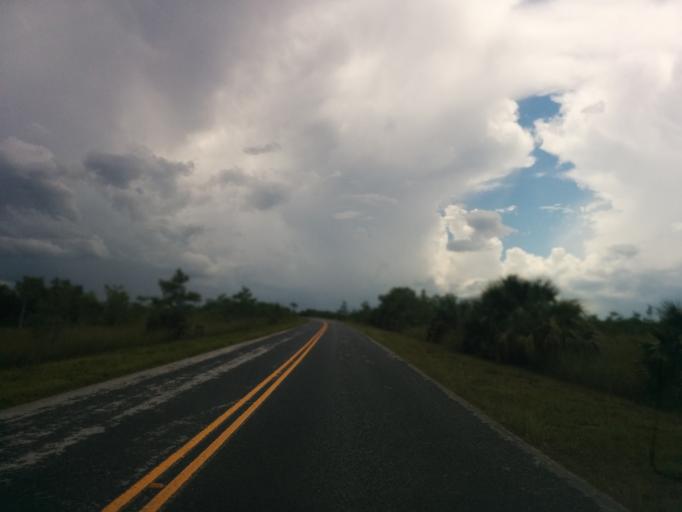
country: US
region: Florida
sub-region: Miami-Dade County
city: Florida City
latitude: 25.4332
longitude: -80.7585
